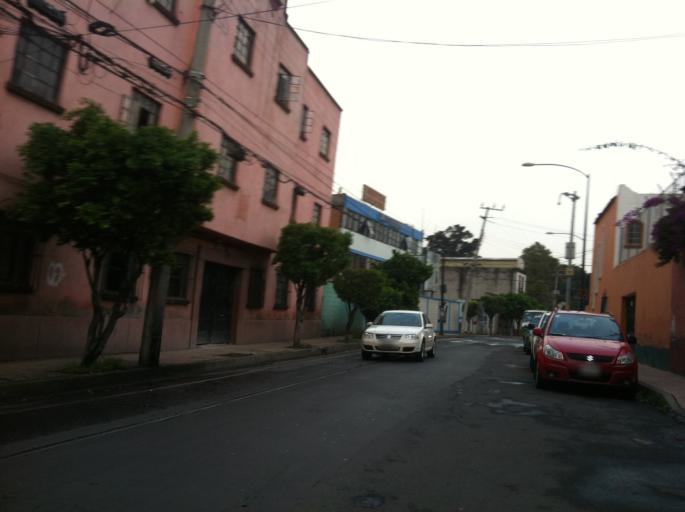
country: MX
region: Mexico City
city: Azcapotzalco
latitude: 19.4585
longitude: -99.1818
